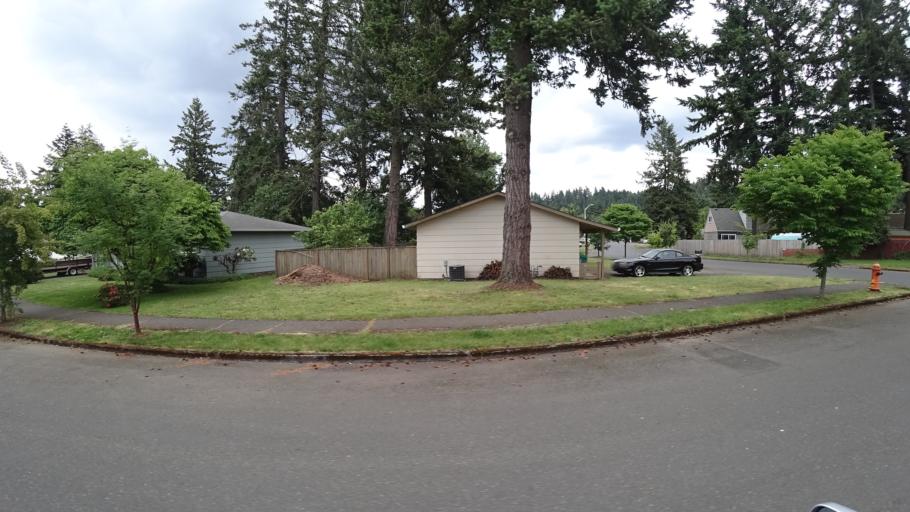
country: US
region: Oregon
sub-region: Clackamas County
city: Happy Valley
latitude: 45.4992
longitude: -122.5008
